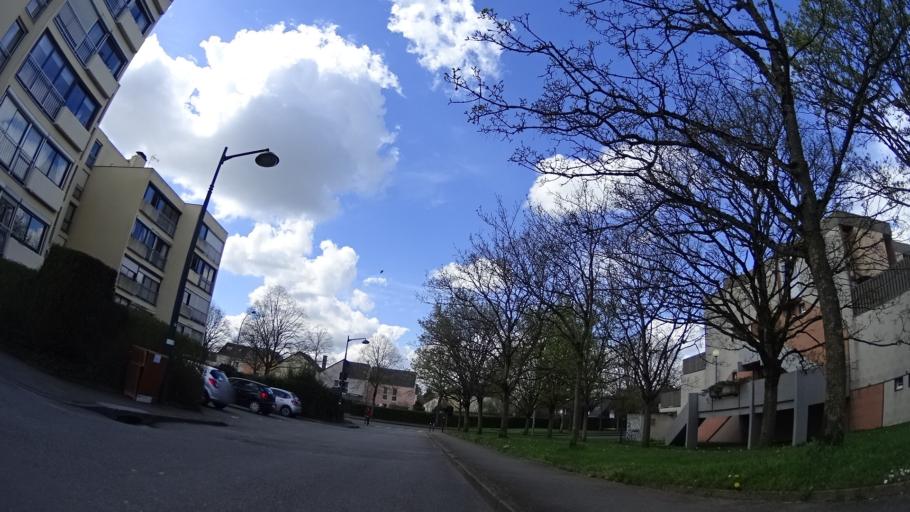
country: FR
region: Brittany
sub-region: Departement d'Ille-et-Vilaine
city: Rennes
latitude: 48.1340
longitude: -1.6667
